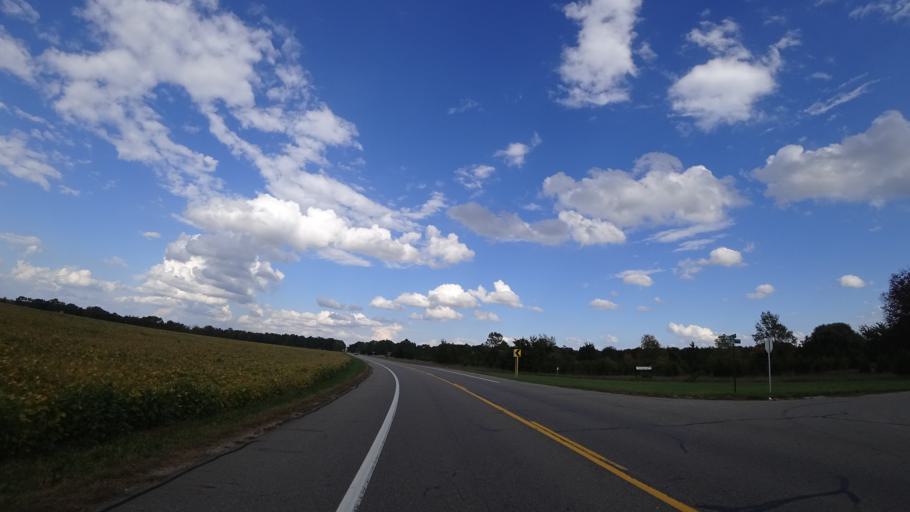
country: US
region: Michigan
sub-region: Saint Joseph County
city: Three Rivers
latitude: 41.9553
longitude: -85.5857
